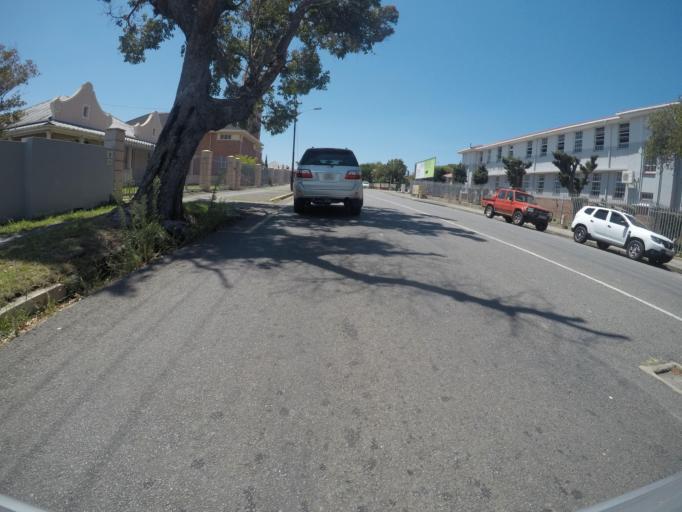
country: ZA
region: Eastern Cape
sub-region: Buffalo City Metropolitan Municipality
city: East London
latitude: -32.9854
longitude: 27.9109
